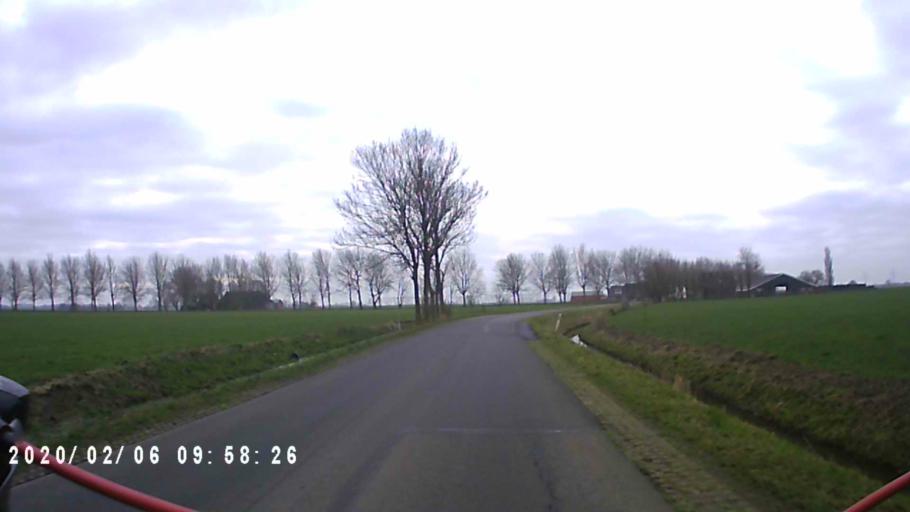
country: NL
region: Groningen
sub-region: Gemeente Zuidhorn
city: Aduard
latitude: 53.2713
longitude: 6.4960
